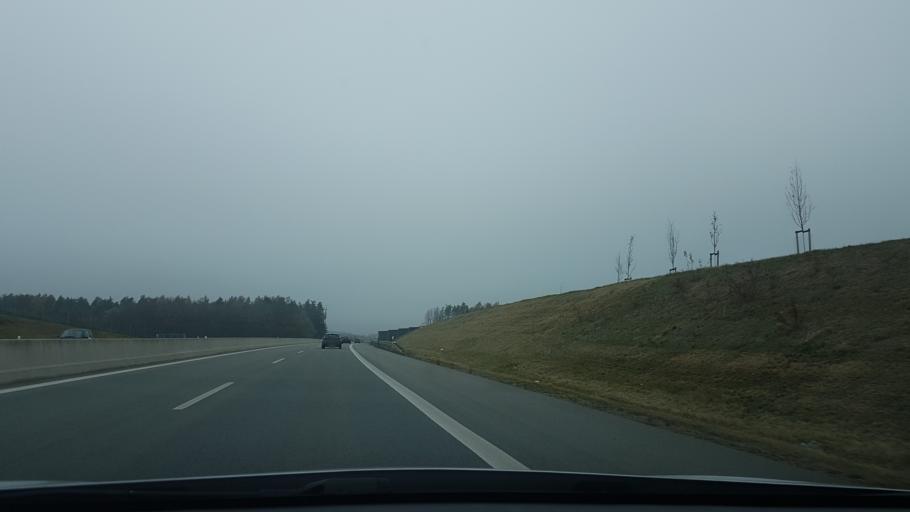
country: DE
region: Bavaria
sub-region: Lower Bavaria
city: Ergoldsbach
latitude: 48.6923
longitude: 12.1809
